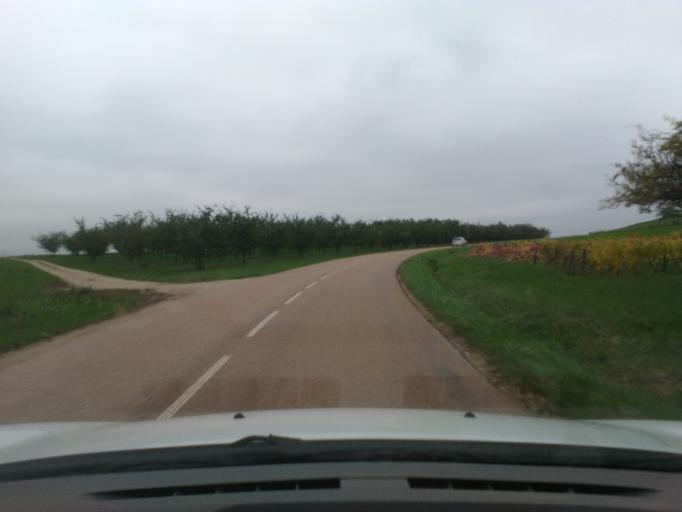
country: FR
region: Lorraine
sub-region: Departement des Vosges
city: Charmes
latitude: 48.3006
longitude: 6.2577
